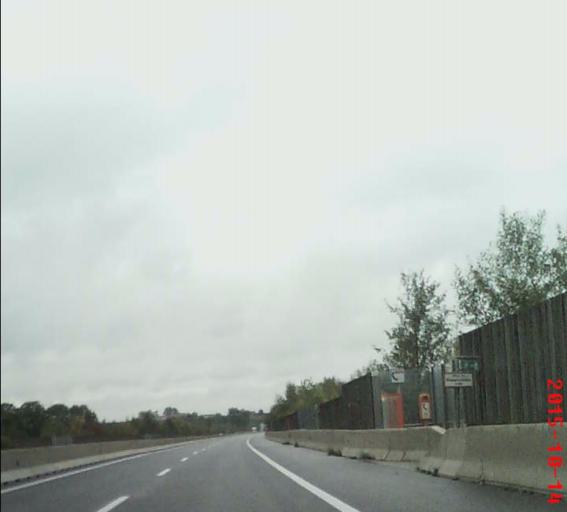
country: AT
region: Upper Austria
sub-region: Politischer Bezirk Kirchdorf an der Krems
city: Micheldorf in Oberoesterreich
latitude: 47.9079
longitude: 14.1010
